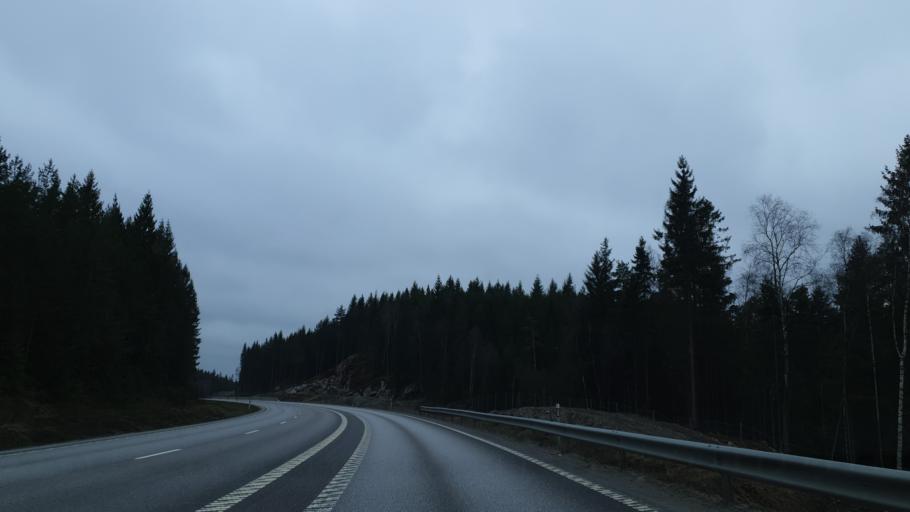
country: SE
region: Vaestra Goetaland
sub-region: Boras Kommun
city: Boras
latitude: 57.6710
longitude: 12.9191
